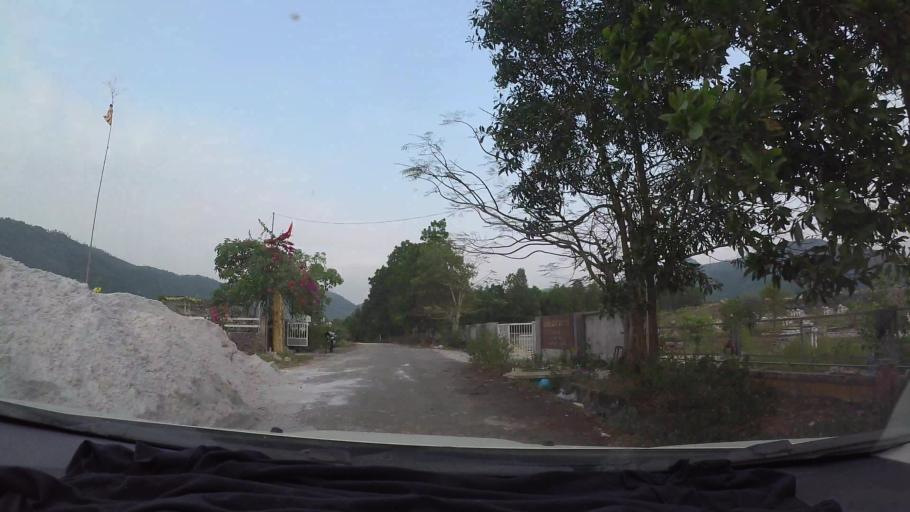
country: VN
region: Da Nang
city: Lien Chieu
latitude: 16.0572
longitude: 108.1099
